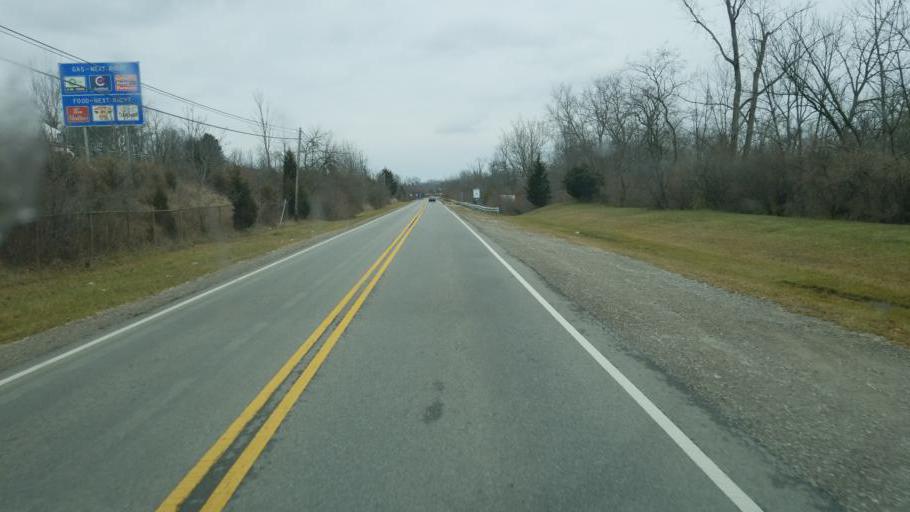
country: US
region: Ohio
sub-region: Delaware County
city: Delaware
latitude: 40.2817
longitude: -83.0668
